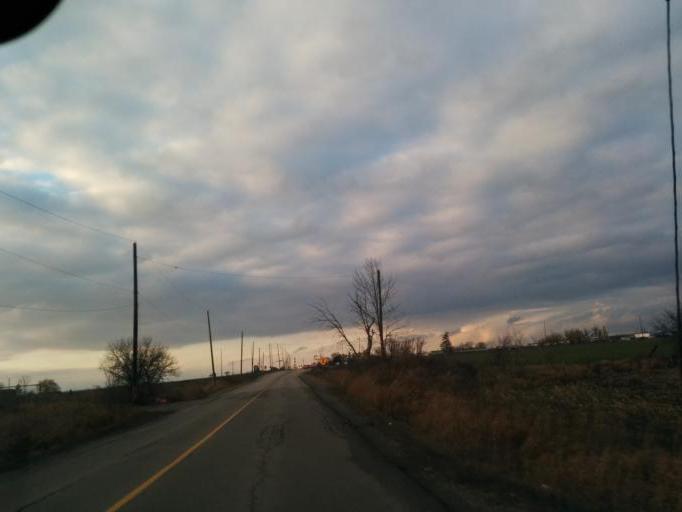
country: CA
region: Ontario
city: Brampton
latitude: 43.8365
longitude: -79.7027
